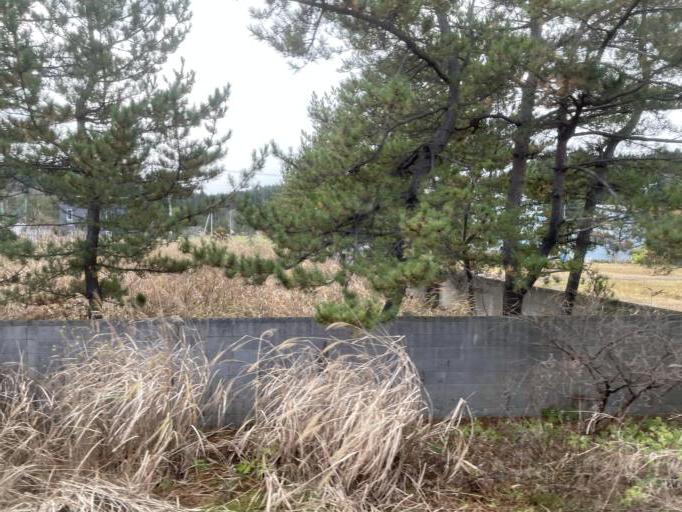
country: JP
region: Aomori
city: Aomori Shi
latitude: 41.0370
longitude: 140.6441
